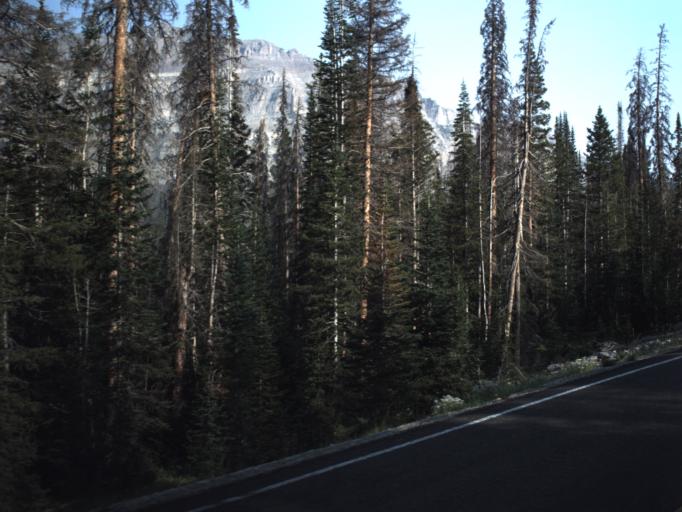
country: US
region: Utah
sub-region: Summit County
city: Kamas
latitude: 40.7441
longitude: -110.8722
